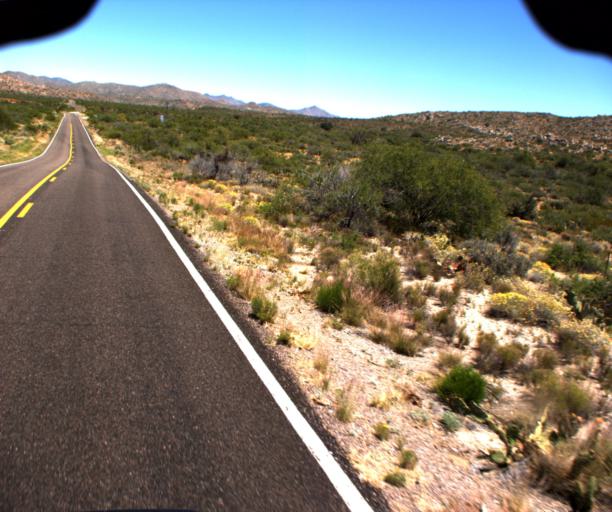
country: US
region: Arizona
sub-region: Yavapai County
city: Bagdad
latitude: 34.5075
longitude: -113.1531
